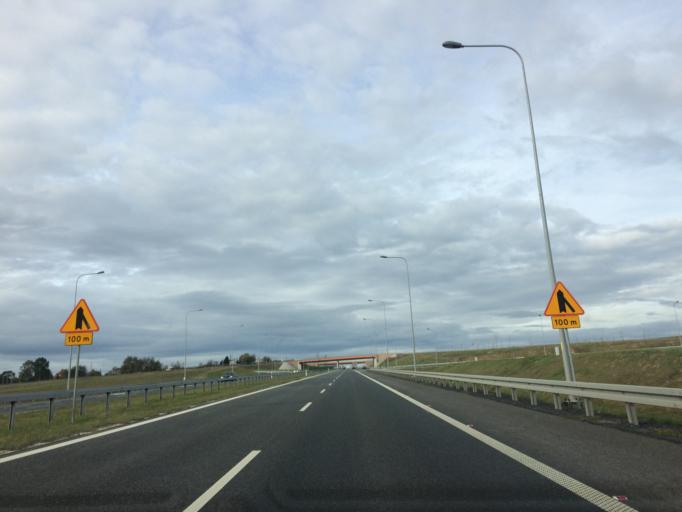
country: PL
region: Lower Silesian Voivodeship
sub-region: Legnica
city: Legnica
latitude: 51.1707
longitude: 16.0967
